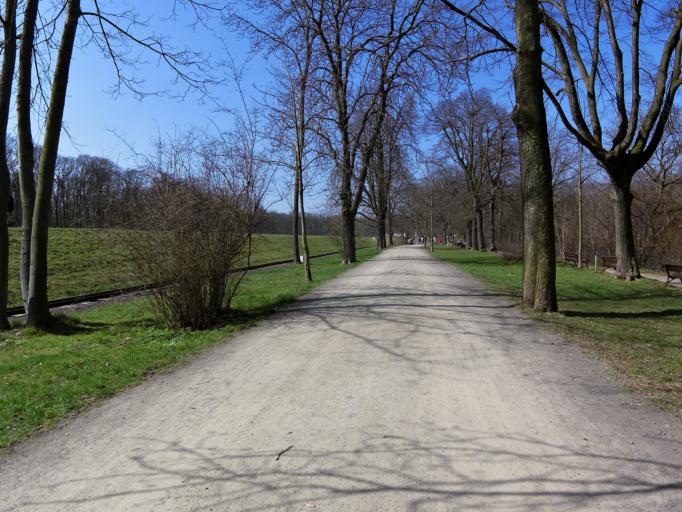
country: DE
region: Saxony
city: Leipzig
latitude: 51.3677
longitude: 12.3172
